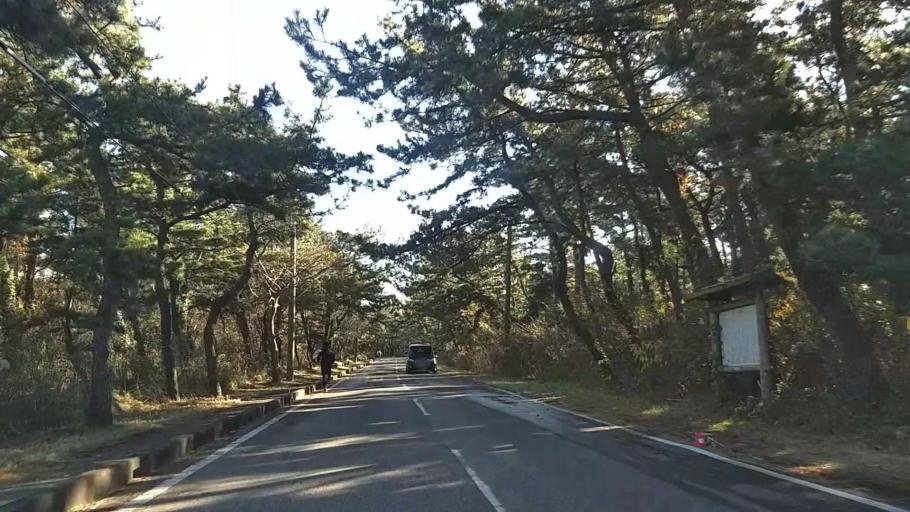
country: JP
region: Chiba
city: Futtsu
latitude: 35.3124
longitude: 139.7991
